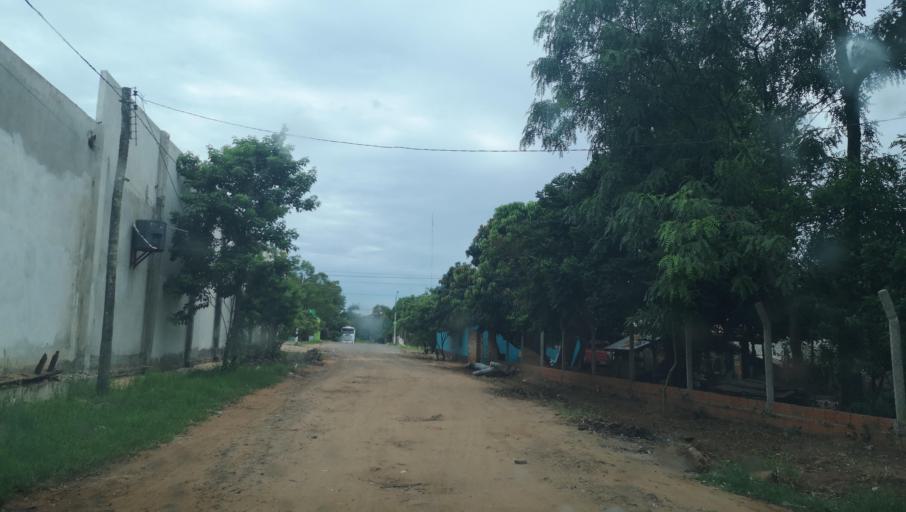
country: PY
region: San Pedro
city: Capiibary
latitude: -24.7415
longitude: -56.0240
